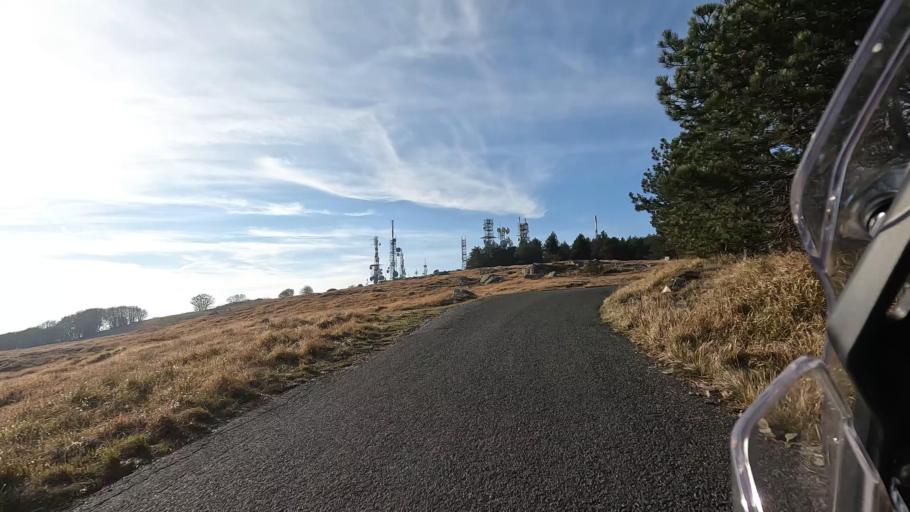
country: IT
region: Liguria
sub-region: Provincia di Genova
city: Sciarborasca
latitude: 44.4318
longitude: 8.5708
